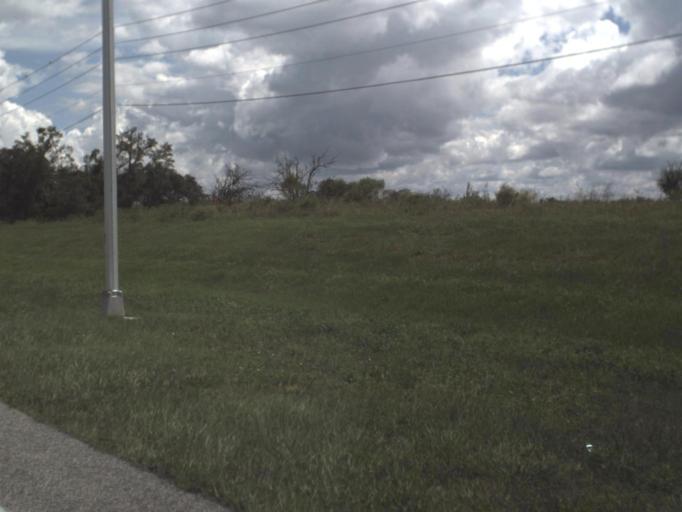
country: US
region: Florida
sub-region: Polk County
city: Babson Park
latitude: 27.8839
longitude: -81.4534
